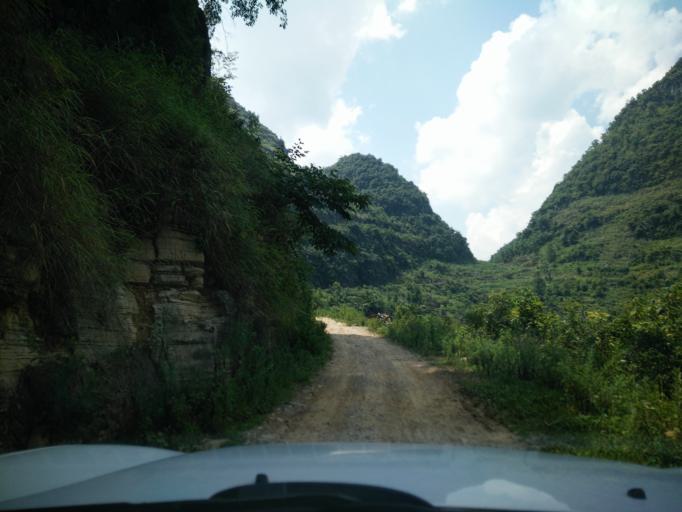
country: CN
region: Guangxi Zhuangzu Zizhiqu
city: Xinzhou
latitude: 25.0211
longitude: 105.7048
